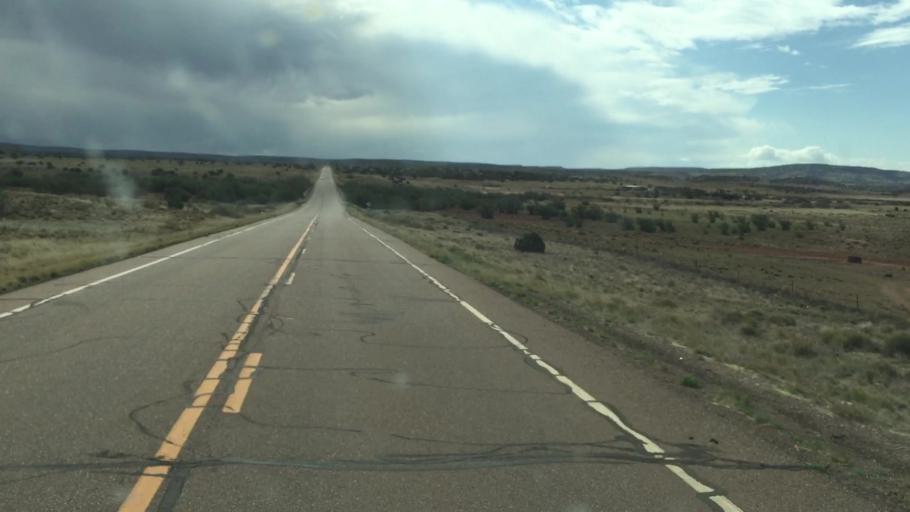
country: US
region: Arizona
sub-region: Navajo County
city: White Mountain Lake
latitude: 34.5155
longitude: -109.7016
